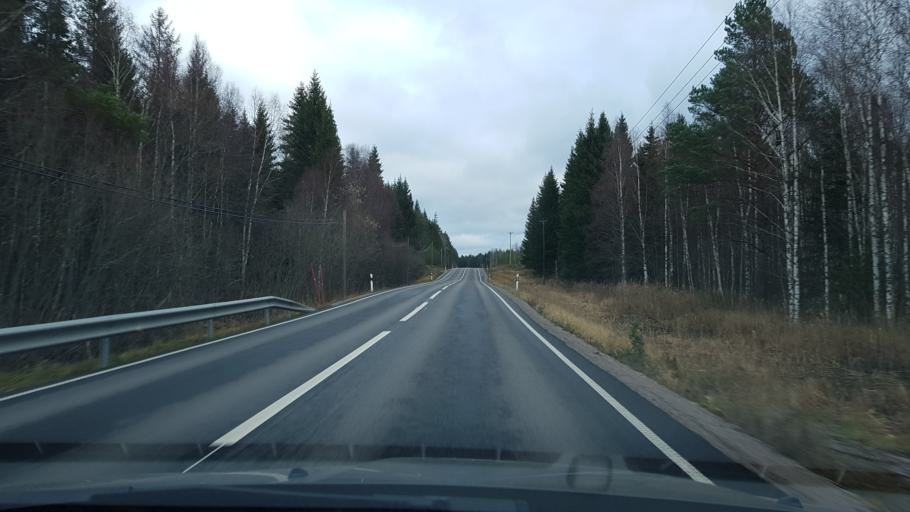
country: SE
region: Stockholm
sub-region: Norrtalje Kommun
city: Skanninge
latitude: 60.0014
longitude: 18.3140
